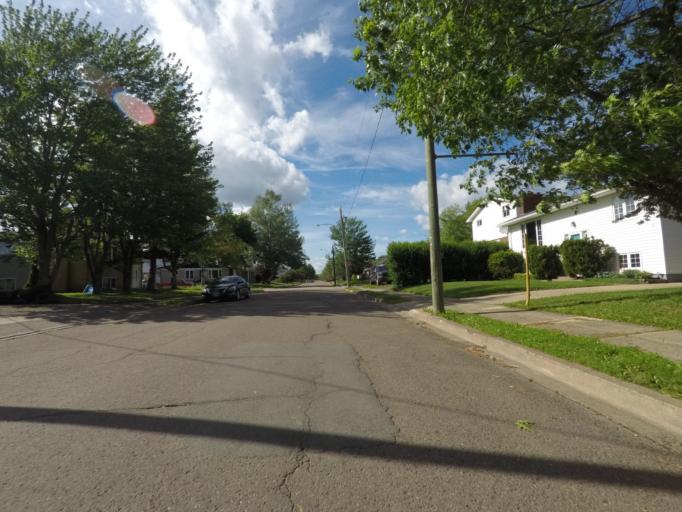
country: CA
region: New Brunswick
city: Moncton
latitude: 46.0984
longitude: -64.8256
